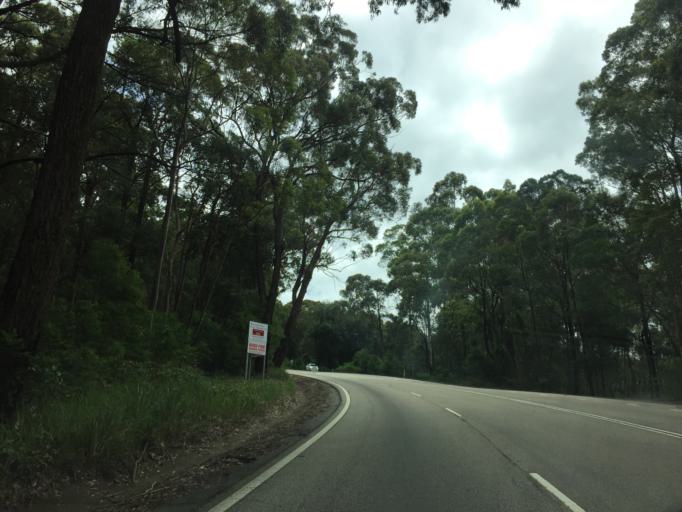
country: AU
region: New South Wales
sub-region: Hawkesbury
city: Richmond
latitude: -33.5411
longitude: 150.6332
